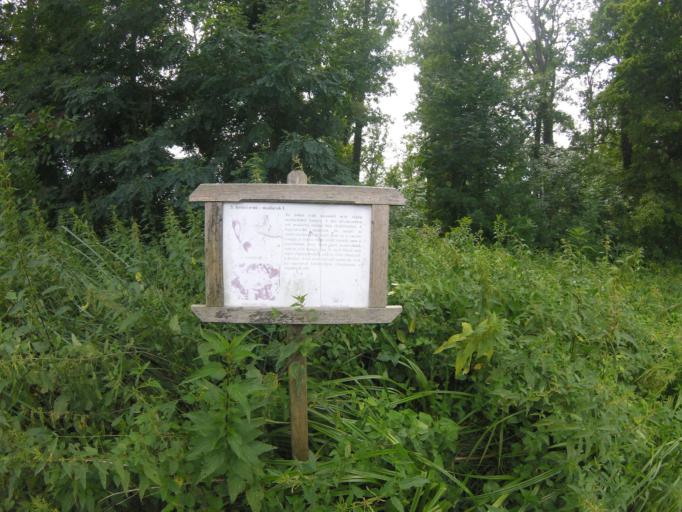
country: HR
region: Medimurska
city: Podturen
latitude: 46.5002
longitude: 16.5784
